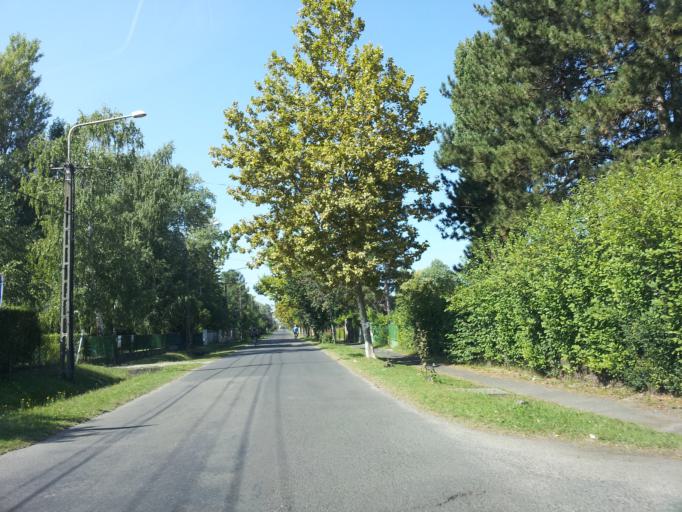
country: HU
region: Somogy
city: Zamardi
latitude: 46.8879
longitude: 17.9650
